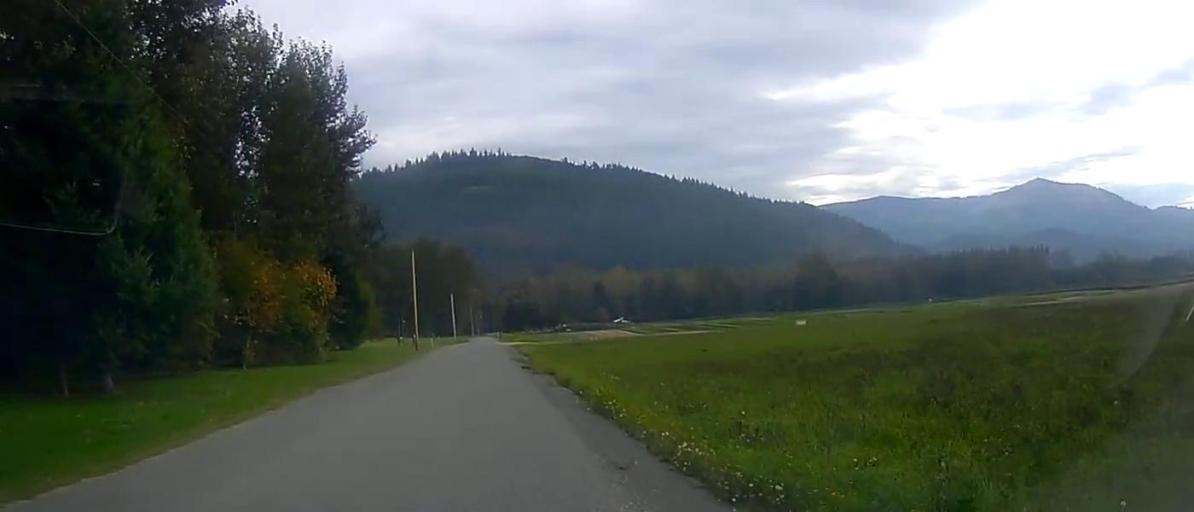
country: US
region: Washington
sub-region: Skagit County
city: Clear Lake
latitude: 48.4787
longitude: -122.2489
